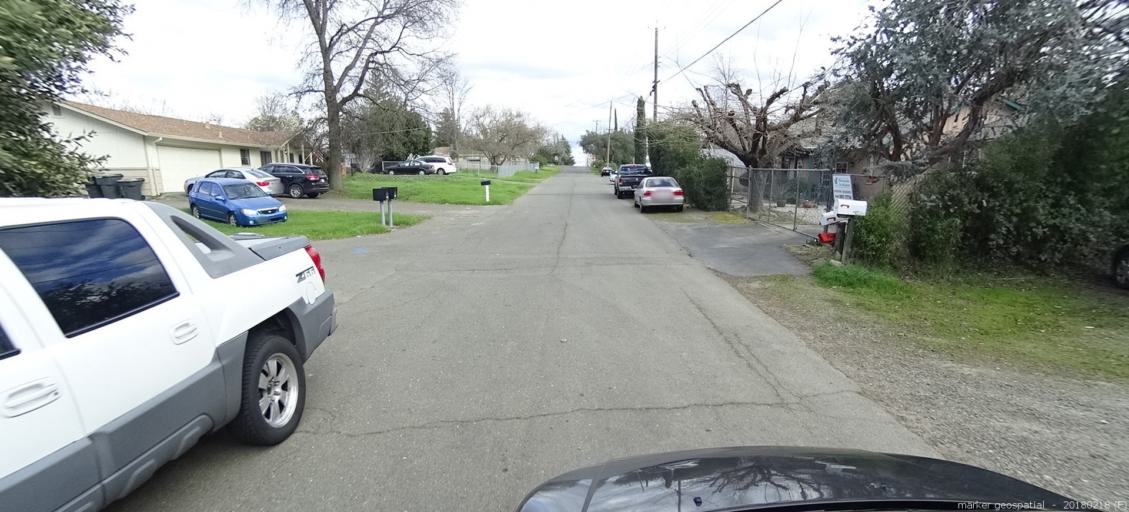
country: US
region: California
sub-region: Sacramento County
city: Orangevale
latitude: 38.6818
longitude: -121.2085
